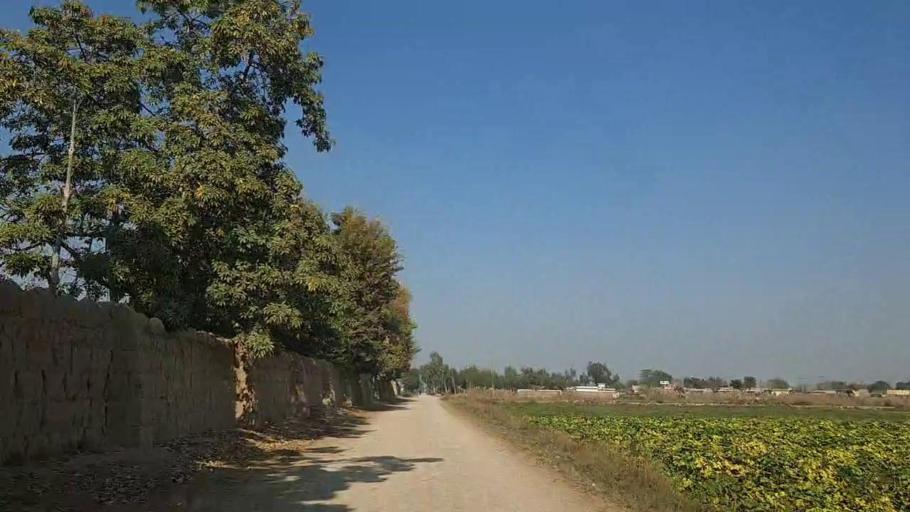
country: PK
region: Sindh
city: Nawabshah
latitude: 26.2450
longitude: 68.3384
